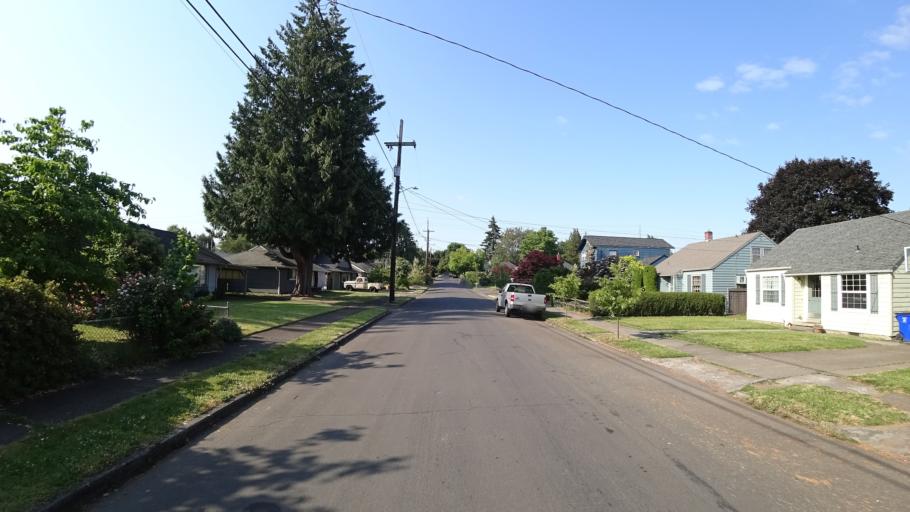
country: US
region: Oregon
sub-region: Washington County
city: West Haven
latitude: 45.5963
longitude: -122.7416
